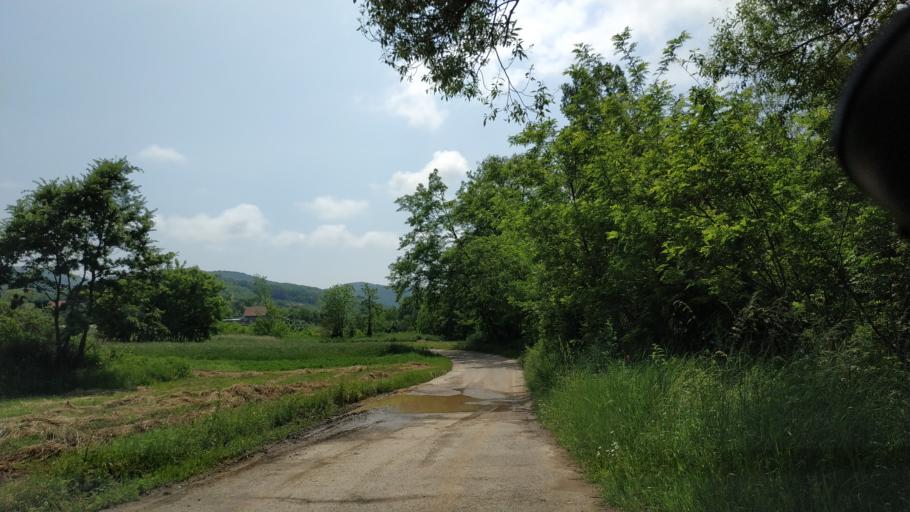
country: RS
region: Central Serbia
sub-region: Nisavski Okrug
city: Aleksinac
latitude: 43.4215
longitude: 21.7180
